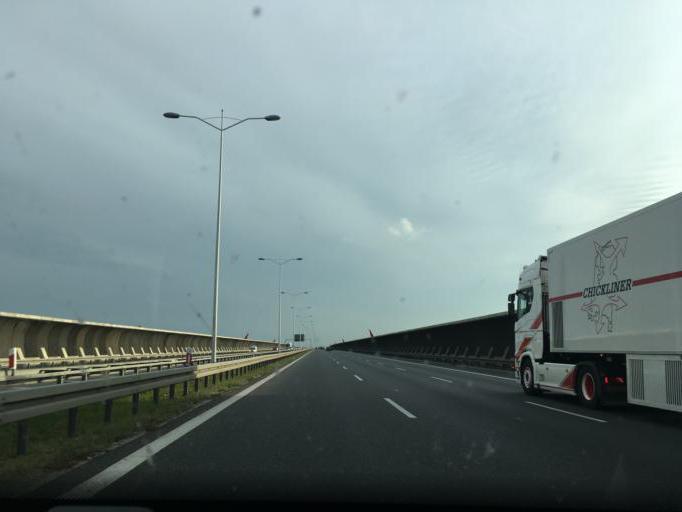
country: PL
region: Lower Silesian Voivodeship
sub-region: Powiat wroclawski
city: Smolec
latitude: 51.0915
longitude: 16.9309
